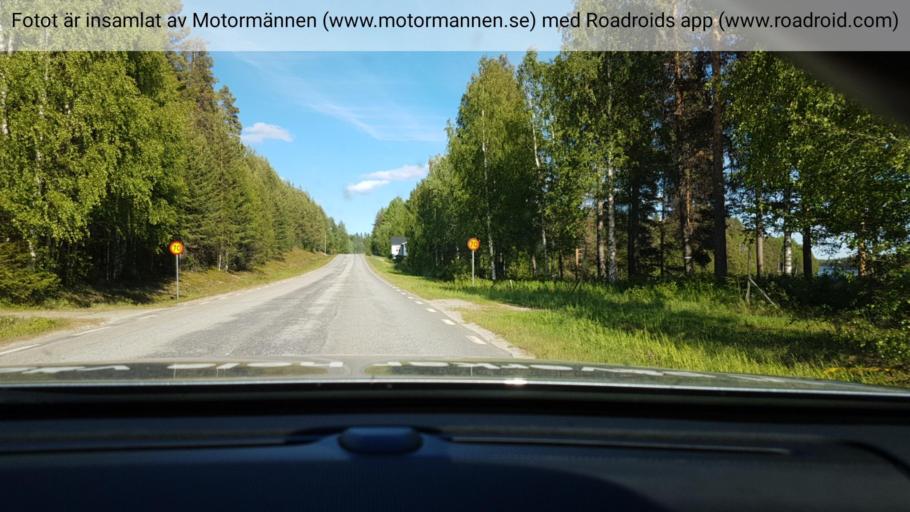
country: SE
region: Vaesterbotten
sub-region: Lycksele Kommun
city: Lycksele
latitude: 64.8169
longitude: 18.8733
